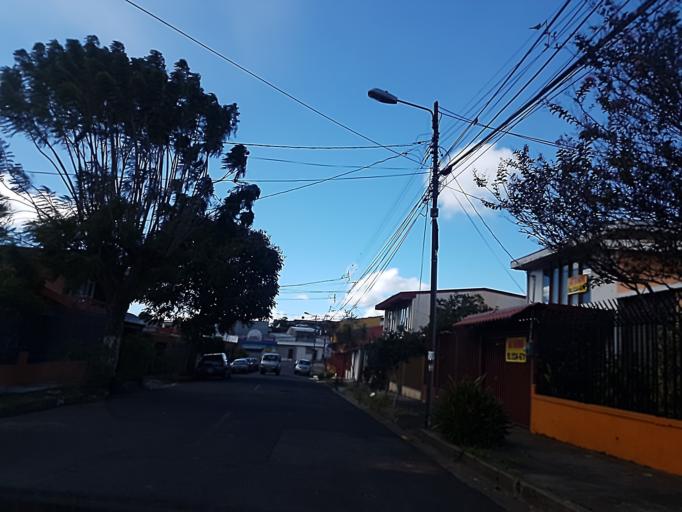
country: CR
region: San Jose
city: San Jose
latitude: 9.9223
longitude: -84.0796
